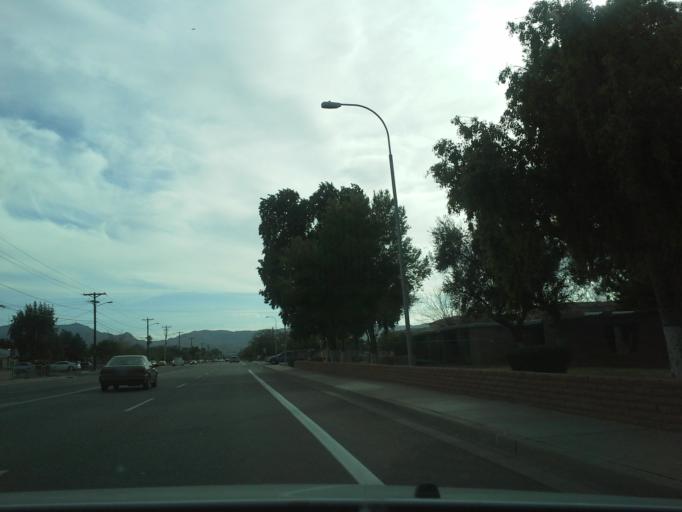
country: US
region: Arizona
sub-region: Maricopa County
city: Phoenix
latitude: 33.3895
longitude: -112.0820
